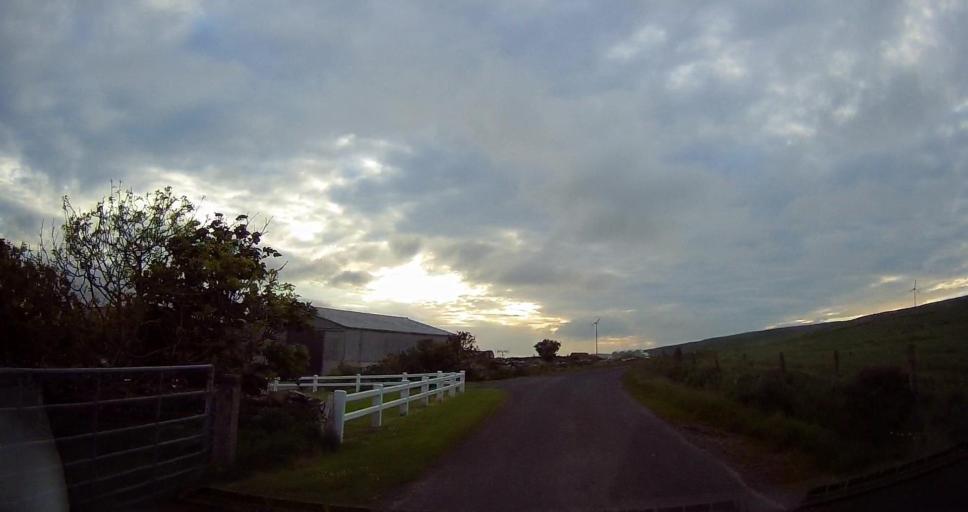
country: GB
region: Scotland
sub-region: Orkney Islands
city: Stromness
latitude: 59.0945
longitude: -3.1880
